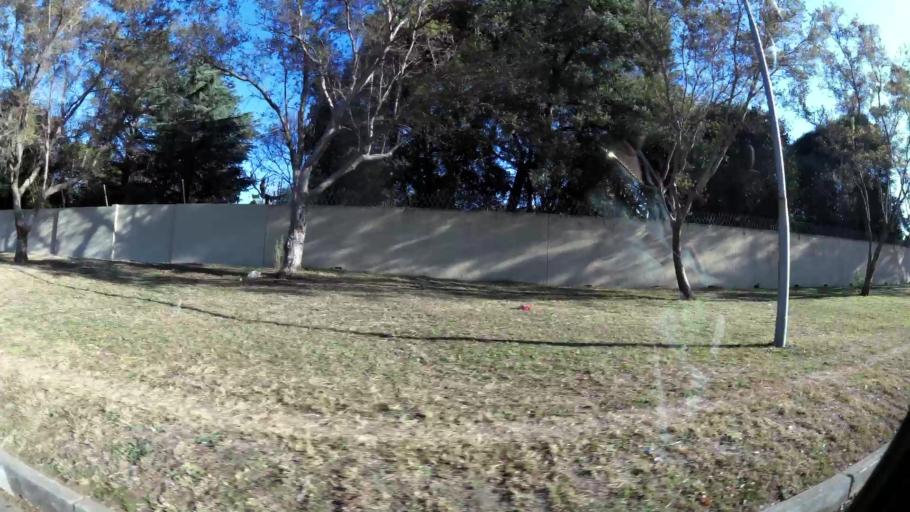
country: ZA
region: Gauteng
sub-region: City of Johannesburg Metropolitan Municipality
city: Midrand
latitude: -26.0293
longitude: 28.0485
